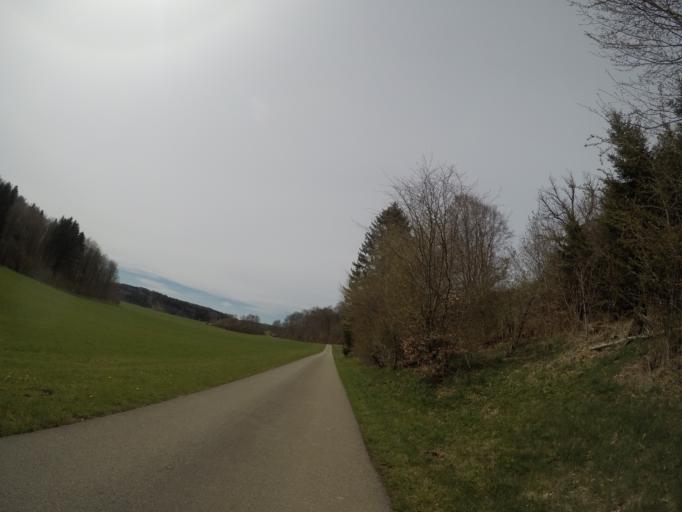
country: DE
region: Baden-Wuerttemberg
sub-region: Regierungsbezirk Stuttgart
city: Neidlingen
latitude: 48.5425
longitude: 9.5593
